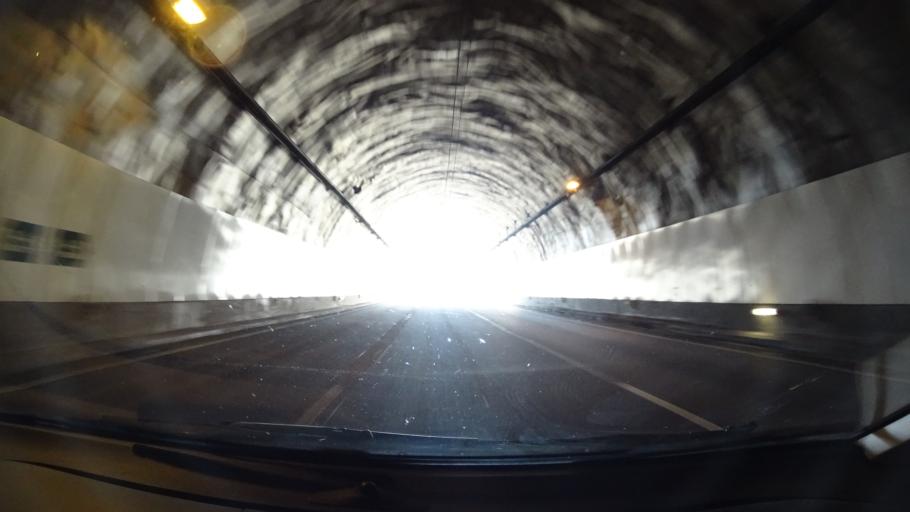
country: ES
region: Andalusia
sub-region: Provincia de Sevilla
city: El Ronquillo
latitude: 37.6441
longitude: -6.1567
